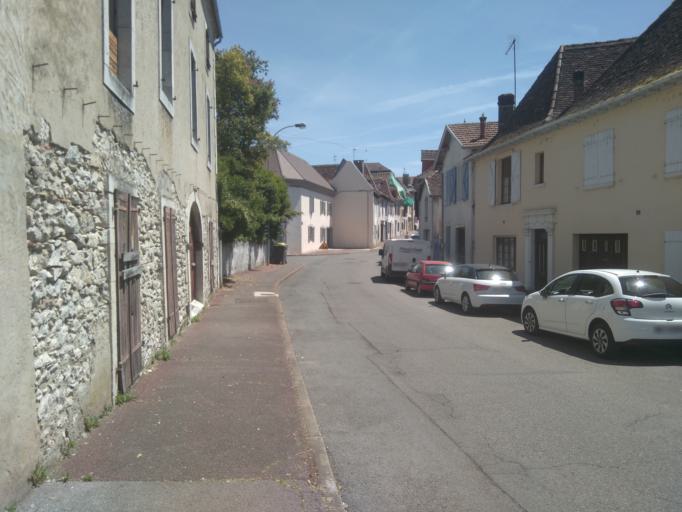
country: FR
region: Aquitaine
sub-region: Departement des Pyrenees-Atlantiques
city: Orthez
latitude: 43.4893
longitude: -0.7775
